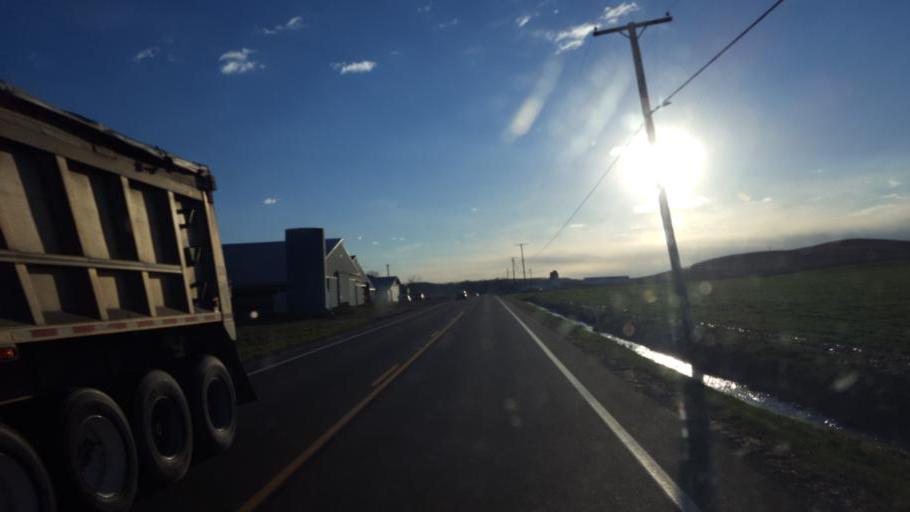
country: US
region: Ohio
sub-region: Ashland County
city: Loudonville
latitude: 40.6530
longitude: -82.2861
